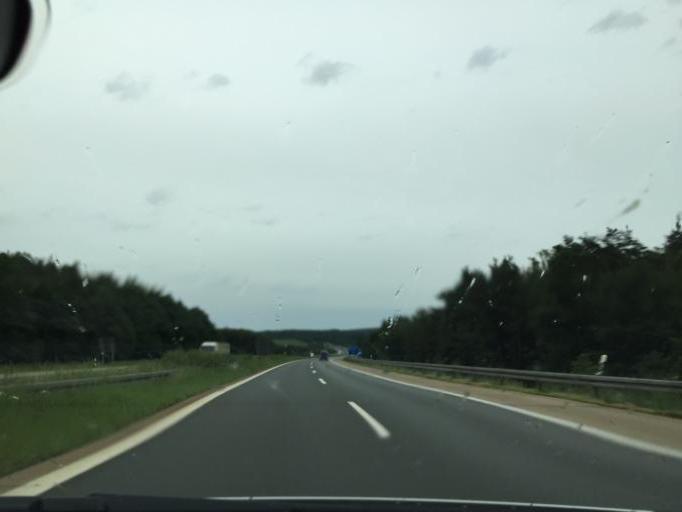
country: DE
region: Bavaria
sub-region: Regierungsbezirk Unterfranken
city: Oberthulba
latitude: 50.2015
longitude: 9.9370
